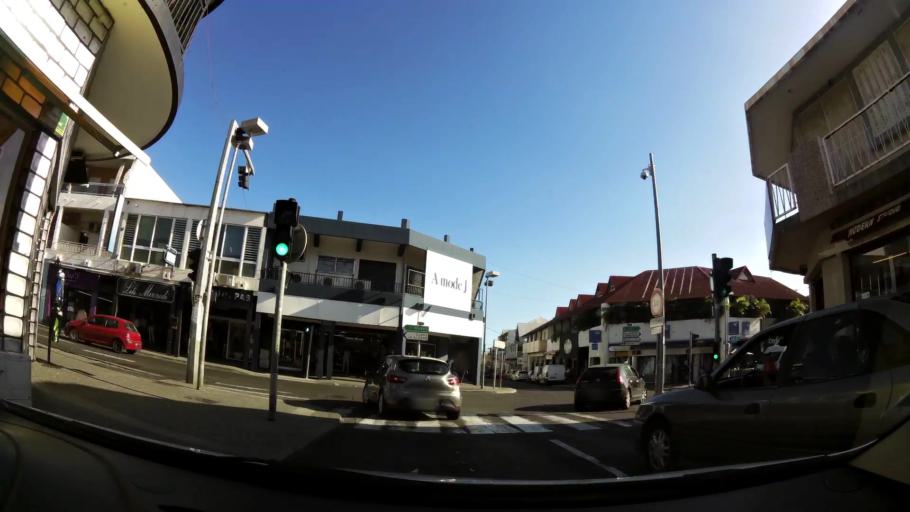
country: RE
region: Reunion
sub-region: Reunion
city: Saint-Louis
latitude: -21.2865
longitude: 55.4080
